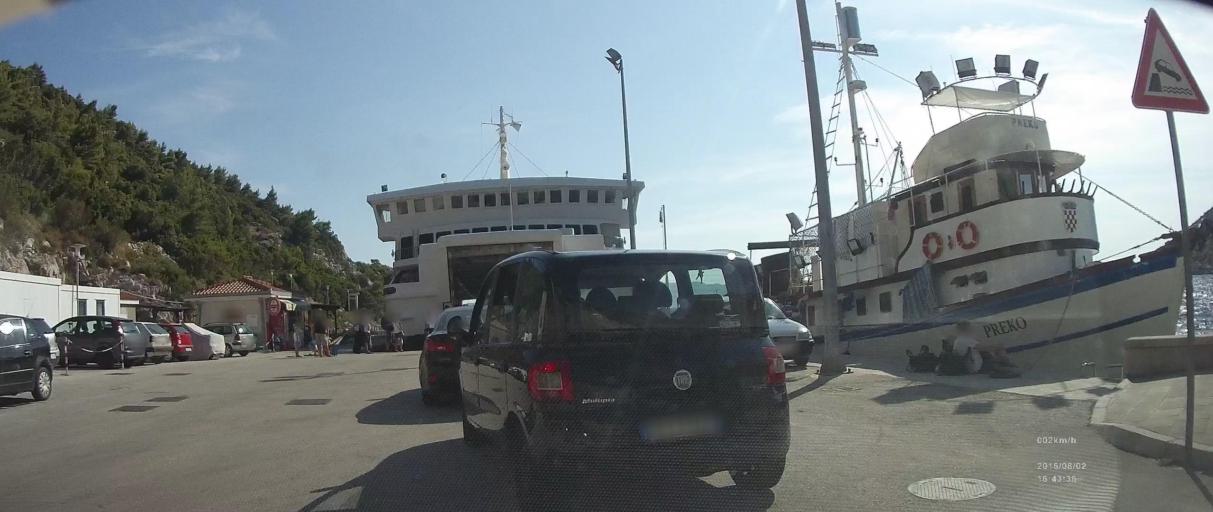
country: HR
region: Dubrovacko-Neretvanska
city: Ston
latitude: 42.8117
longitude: 17.6788
